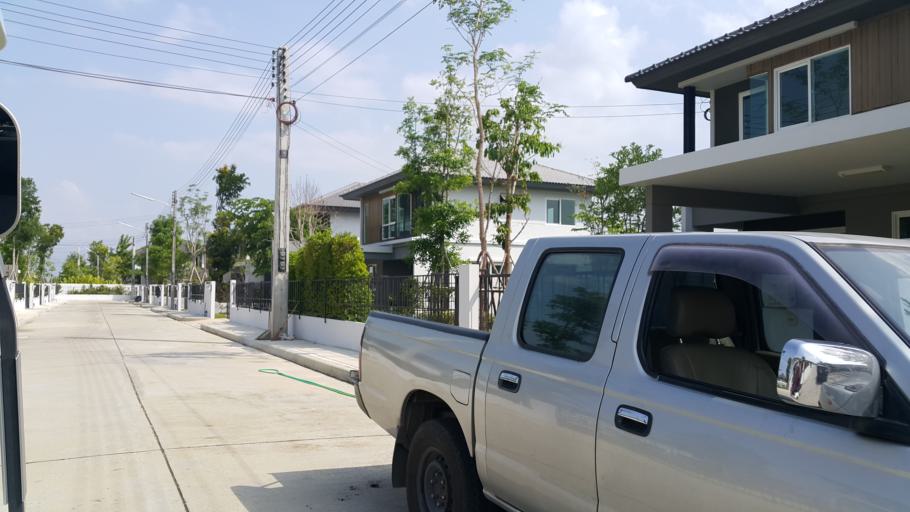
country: TH
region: Chiang Mai
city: San Kamphaeng
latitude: 18.7351
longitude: 99.0856
